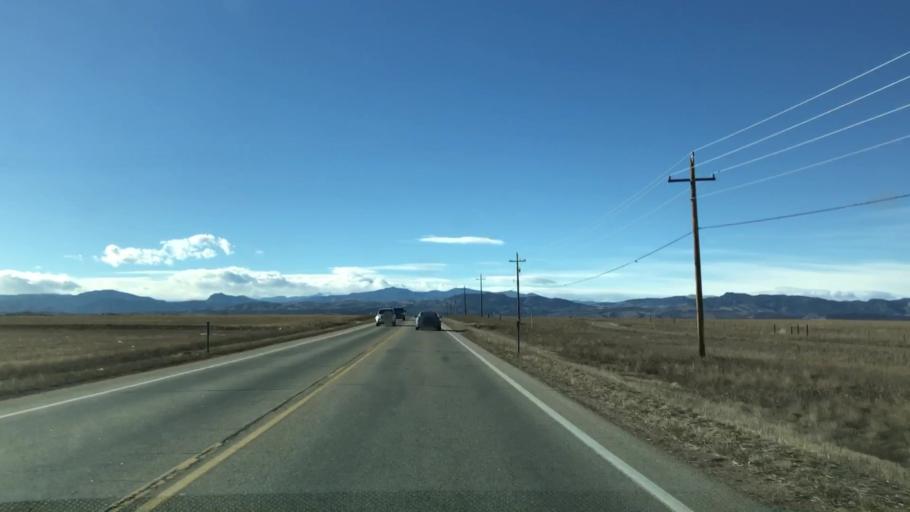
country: US
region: Colorado
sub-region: Larimer County
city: Loveland
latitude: 40.4802
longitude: -105.0124
